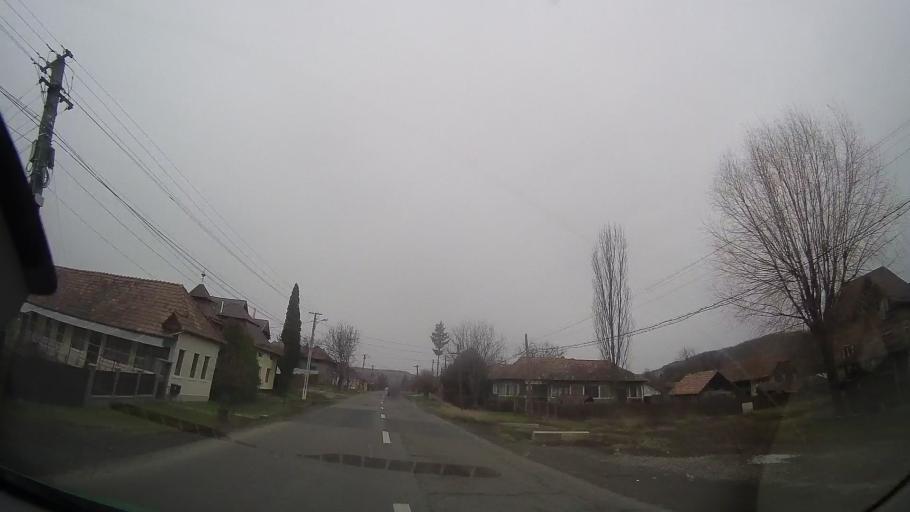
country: RO
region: Mures
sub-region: Comuna Ceausu de Campie
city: Ceausu de Campie
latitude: 46.6429
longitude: 24.5053
